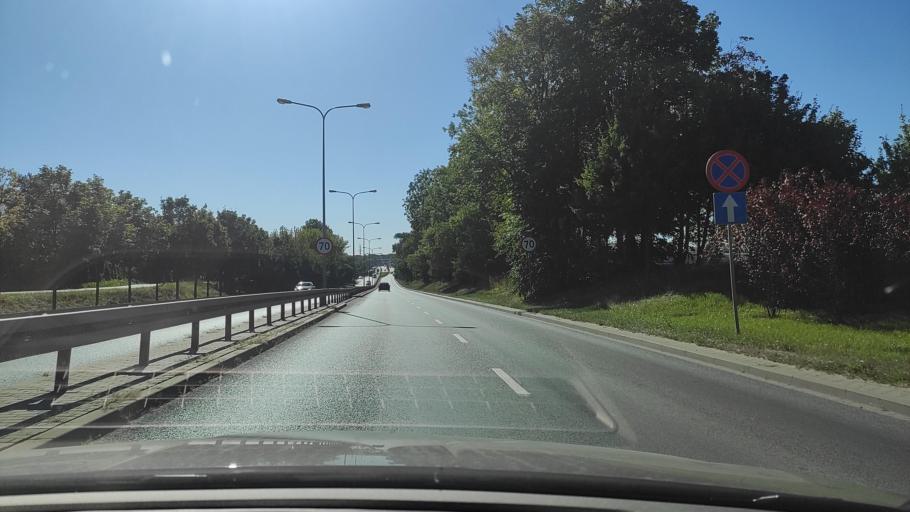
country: PL
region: Greater Poland Voivodeship
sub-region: Poznan
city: Poznan
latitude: 52.4350
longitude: 16.9557
